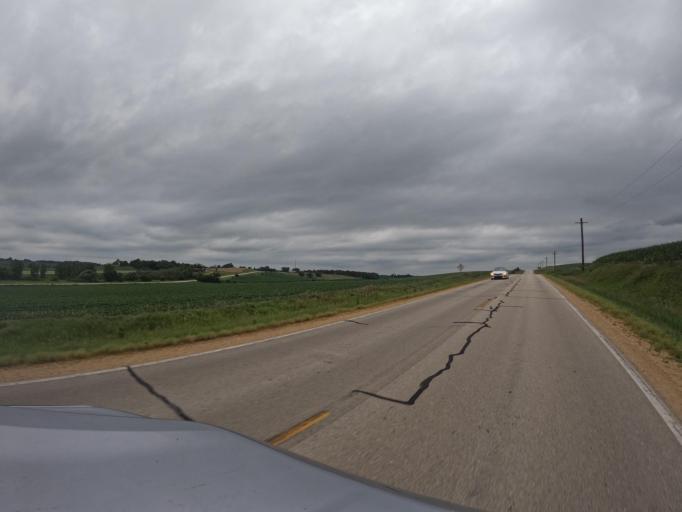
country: US
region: Iowa
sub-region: Clinton County
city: De Witt
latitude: 41.9326
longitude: -90.6065
